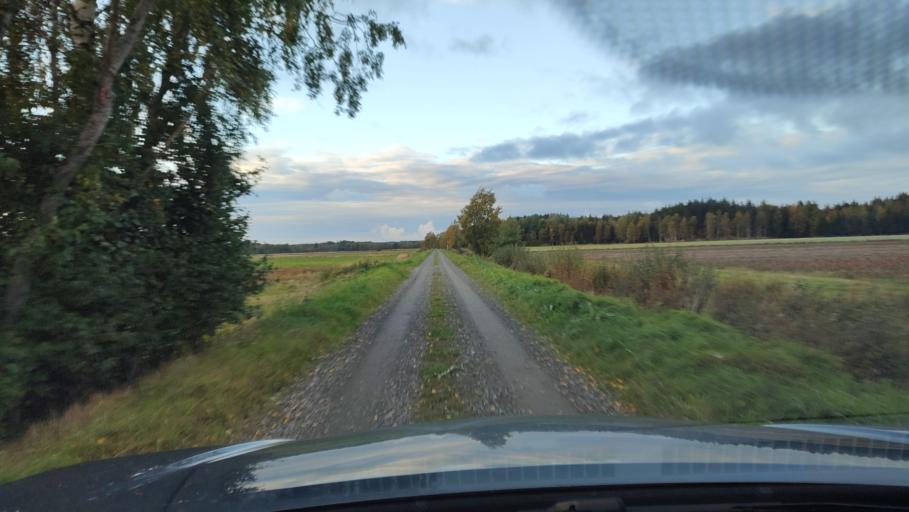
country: FI
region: Ostrobothnia
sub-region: Sydosterbotten
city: Kristinestad
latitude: 62.2406
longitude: 21.4548
